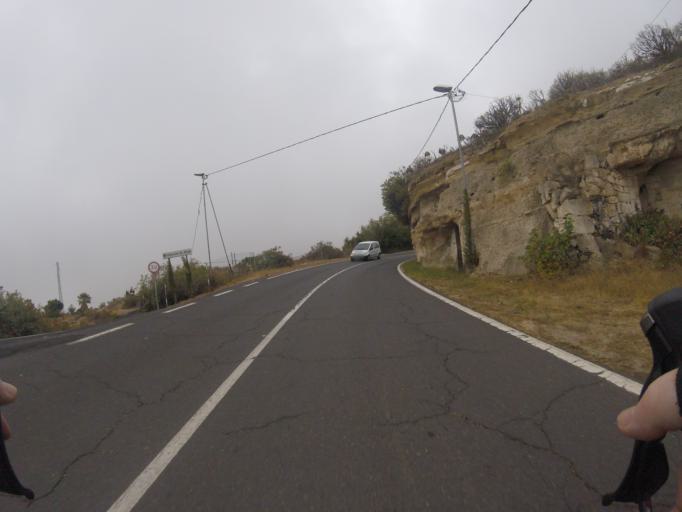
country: ES
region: Canary Islands
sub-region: Provincia de Santa Cruz de Tenerife
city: Guimar
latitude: 28.2819
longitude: -16.4068
